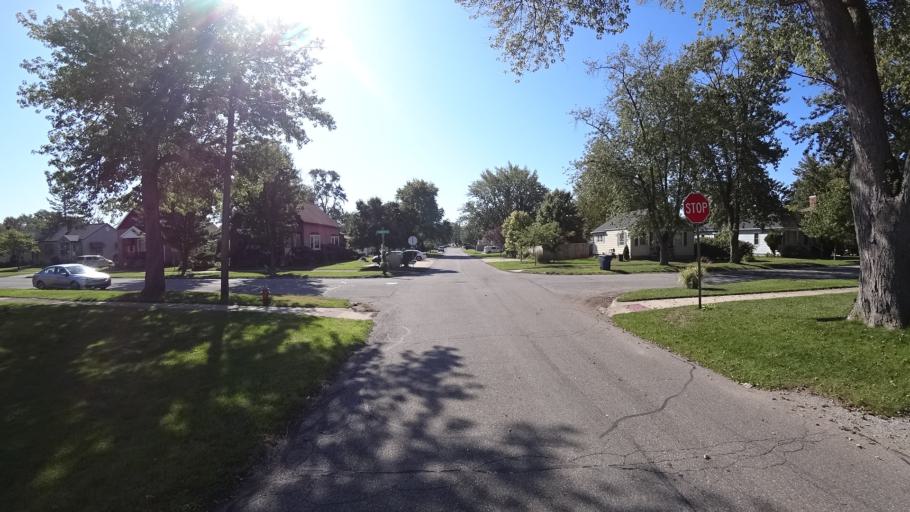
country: US
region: Indiana
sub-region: LaPorte County
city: Michigan City
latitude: 41.7078
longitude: -86.8878
